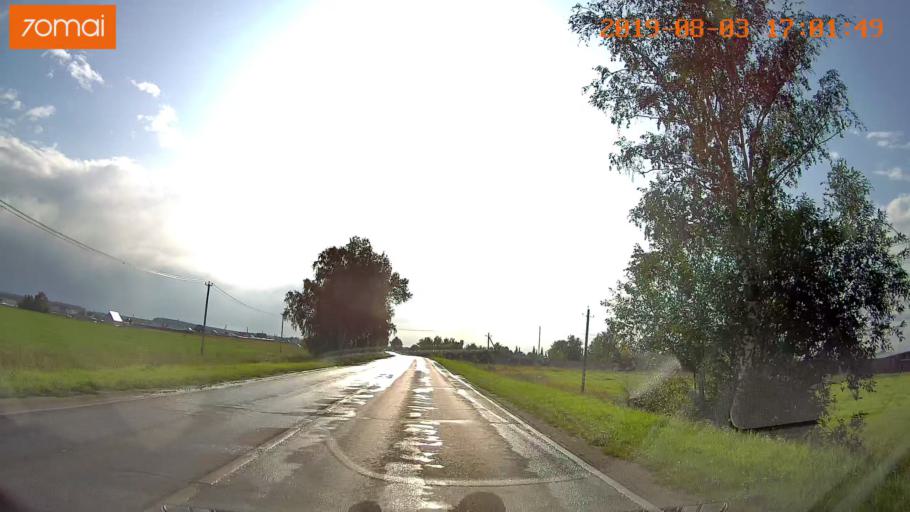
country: RU
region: Moskovskaya
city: Voskresensk
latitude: 55.3467
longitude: 38.5948
